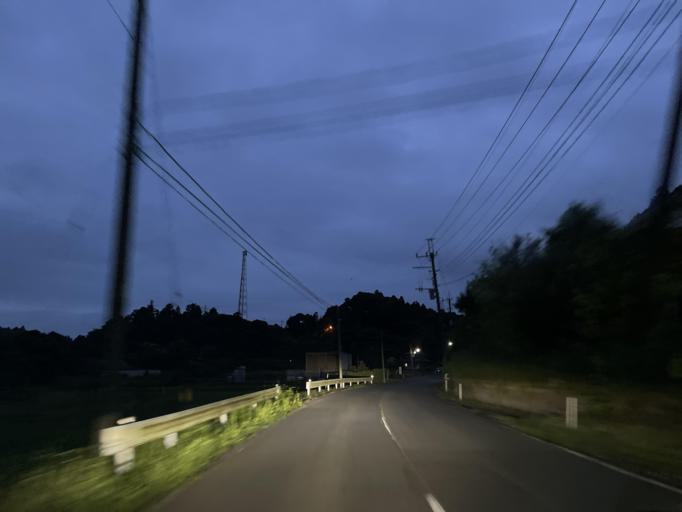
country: JP
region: Chiba
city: Omigawa
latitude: 35.7995
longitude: 140.5987
